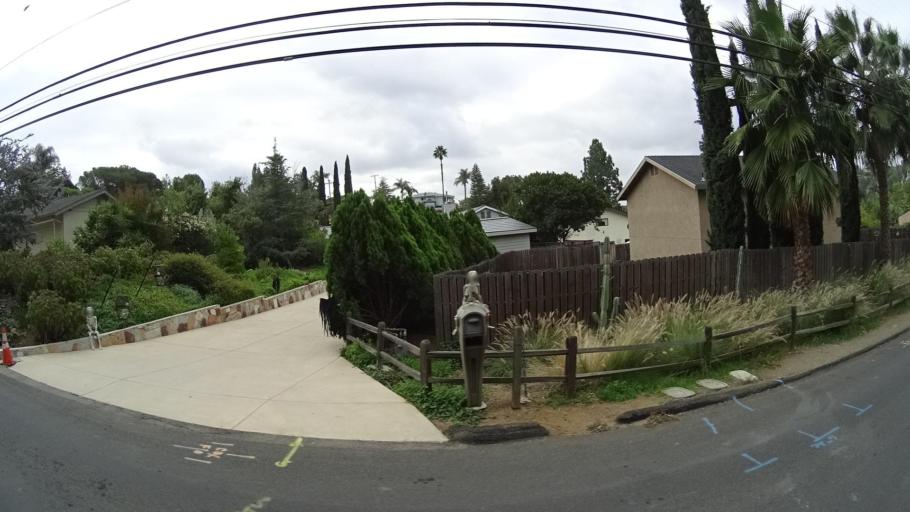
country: US
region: California
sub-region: San Diego County
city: Spring Valley
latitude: 32.7579
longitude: -116.9973
